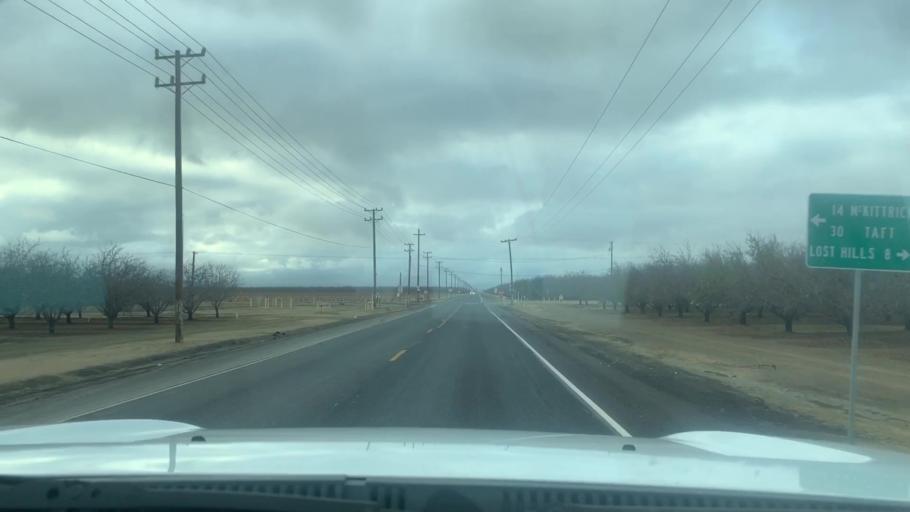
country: US
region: California
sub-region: Kern County
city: Lost Hills
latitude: 35.4992
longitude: -119.6882
